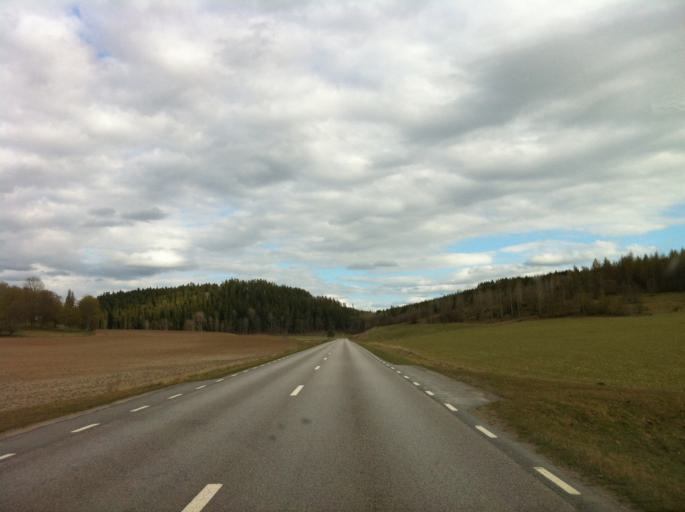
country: SE
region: OEstergoetland
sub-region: Kinda Kommun
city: Rimforsa
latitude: 58.0464
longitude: 15.8452
